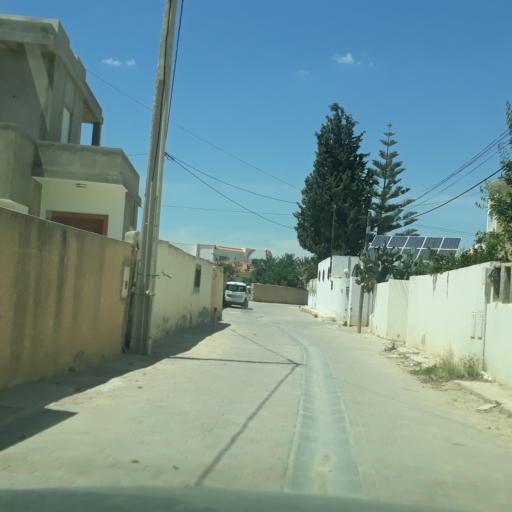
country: TN
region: Safaqis
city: Al Qarmadah
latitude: 34.8078
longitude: 10.7562
